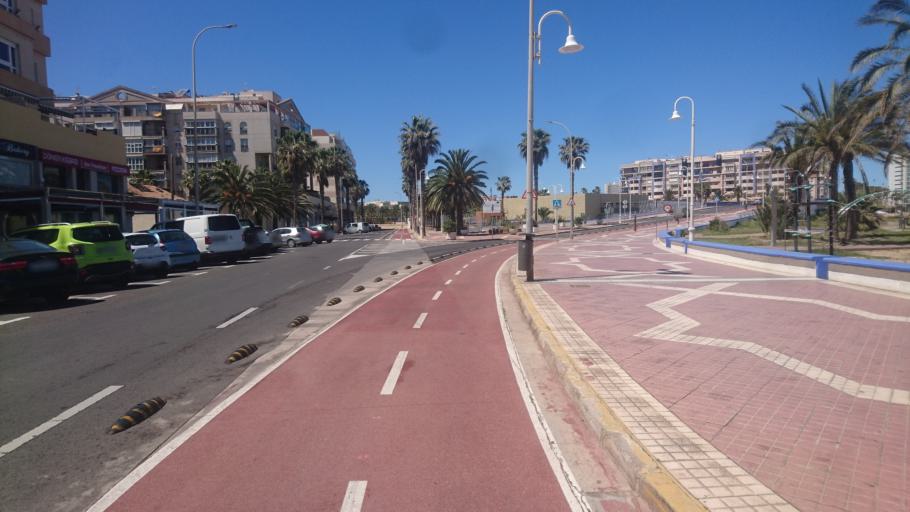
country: ES
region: Melilla
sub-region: Melilla
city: Melilla
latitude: 35.2844
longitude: -2.9389
